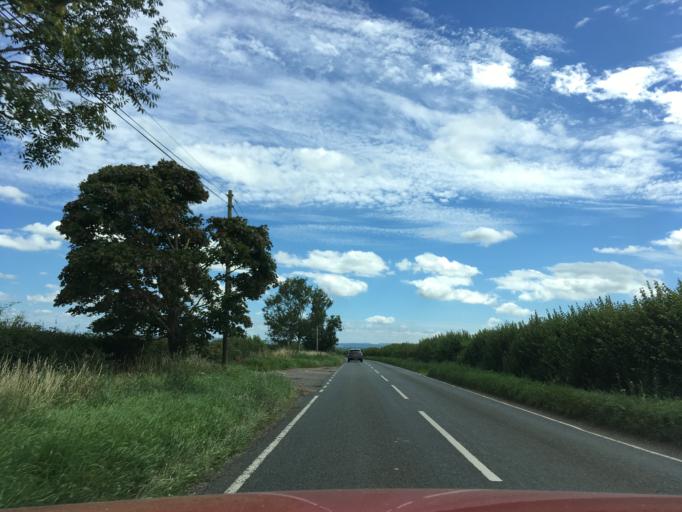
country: GB
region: England
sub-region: Somerset
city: Ilchester
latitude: 51.0664
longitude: -2.6816
